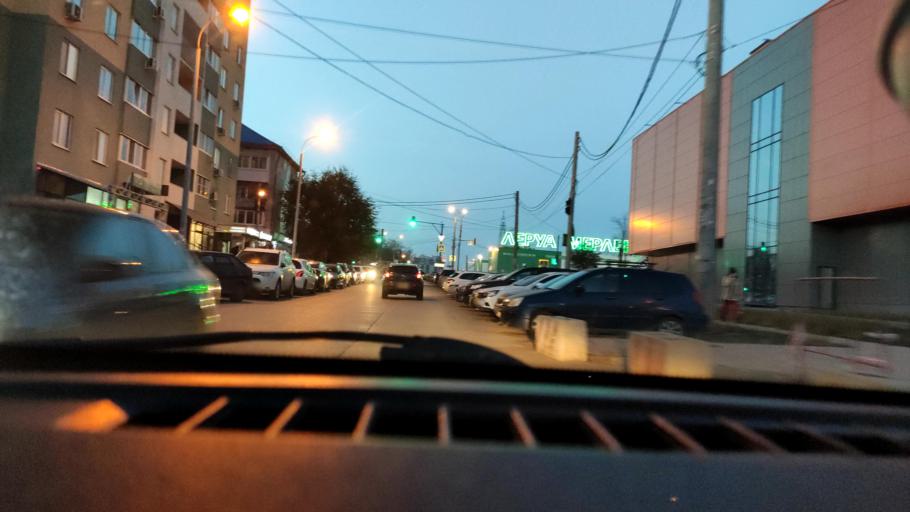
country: RU
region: Samara
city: Samara
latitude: 53.2049
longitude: 50.1939
